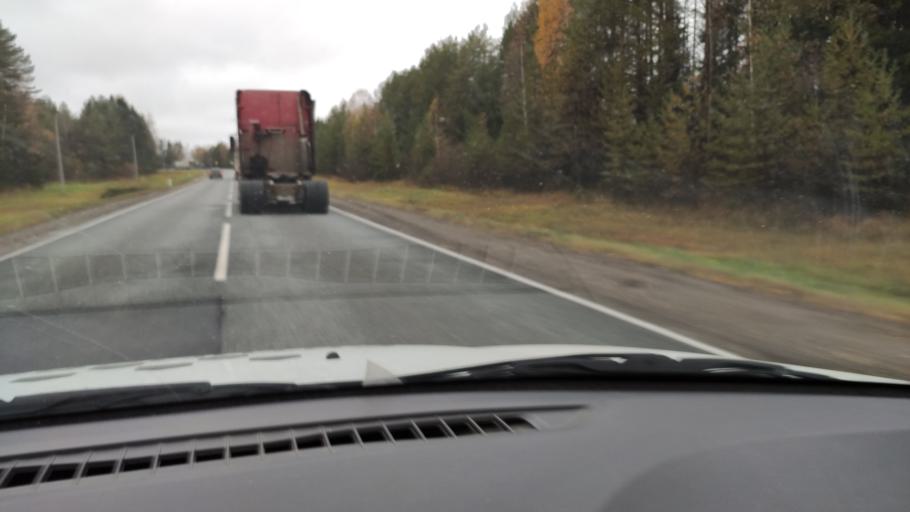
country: RU
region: Kirov
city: Belaya Kholunitsa
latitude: 58.8527
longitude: 50.7337
